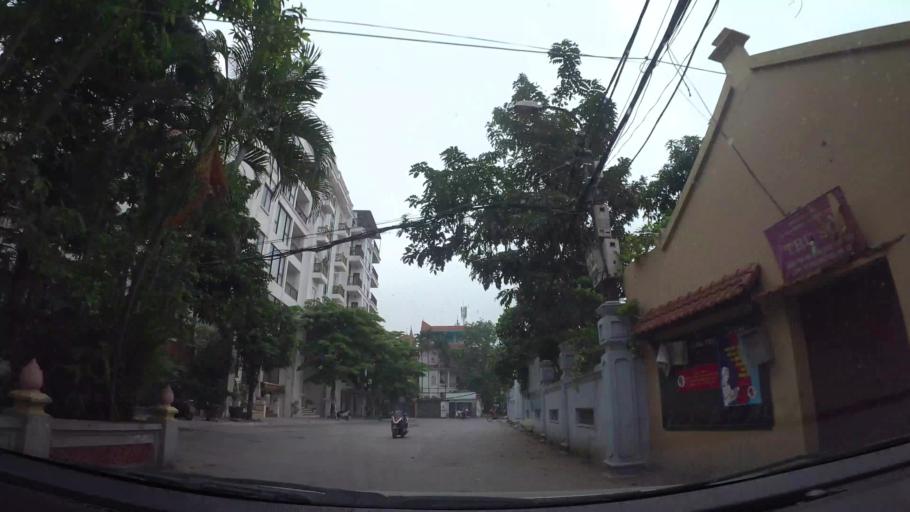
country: VN
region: Ha Noi
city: Tay Ho
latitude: 21.0669
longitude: 105.8229
